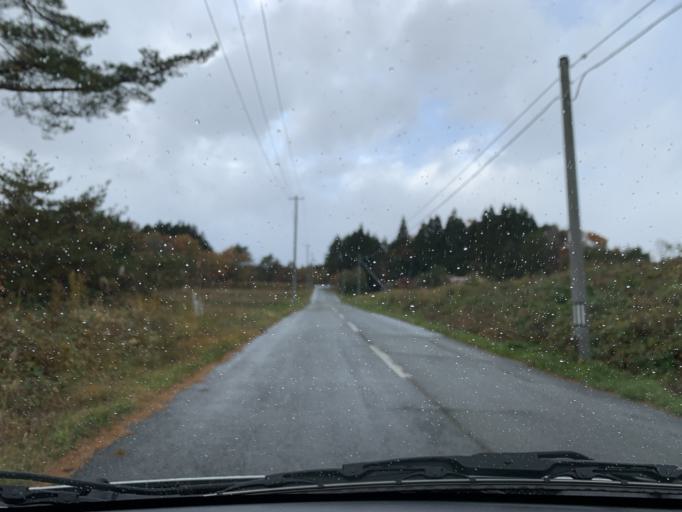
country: JP
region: Iwate
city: Mizusawa
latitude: 39.0972
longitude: 140.9827
